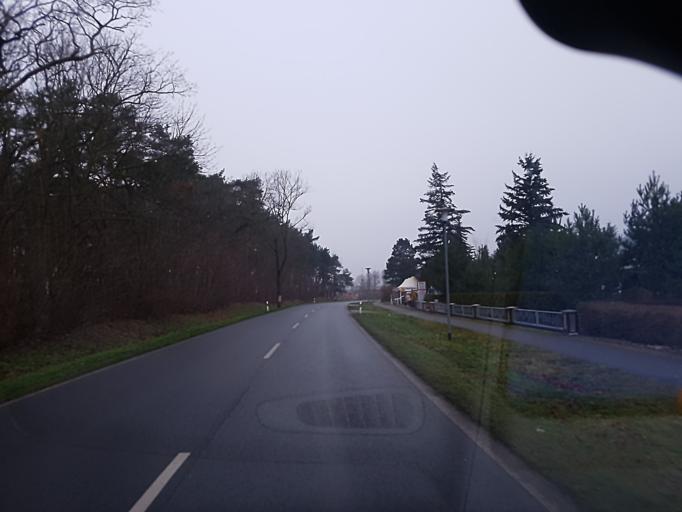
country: DE
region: Brandenburg
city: Lubbenau
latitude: 51.8655
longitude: 13.9229
